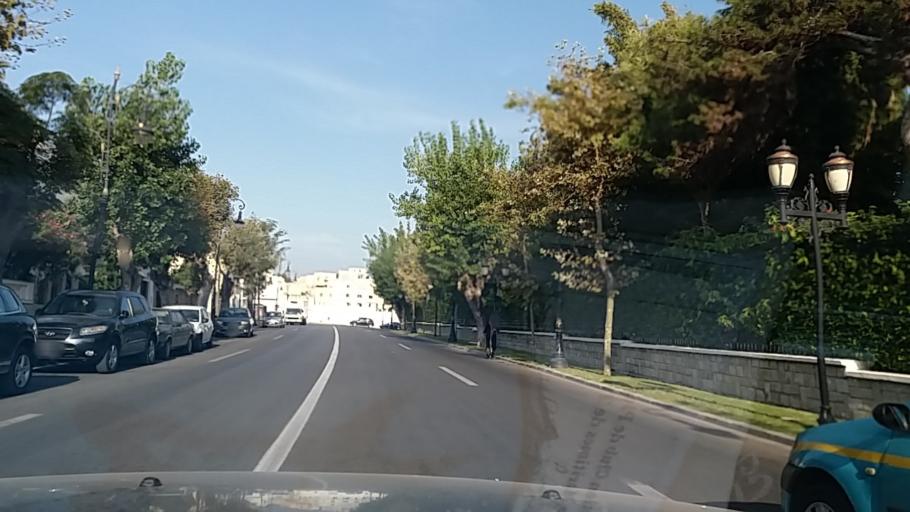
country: MA
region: Tanger-Tetouan
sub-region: Tanger-Assilah
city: Tangier
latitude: 35.7902
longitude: -5.8268
